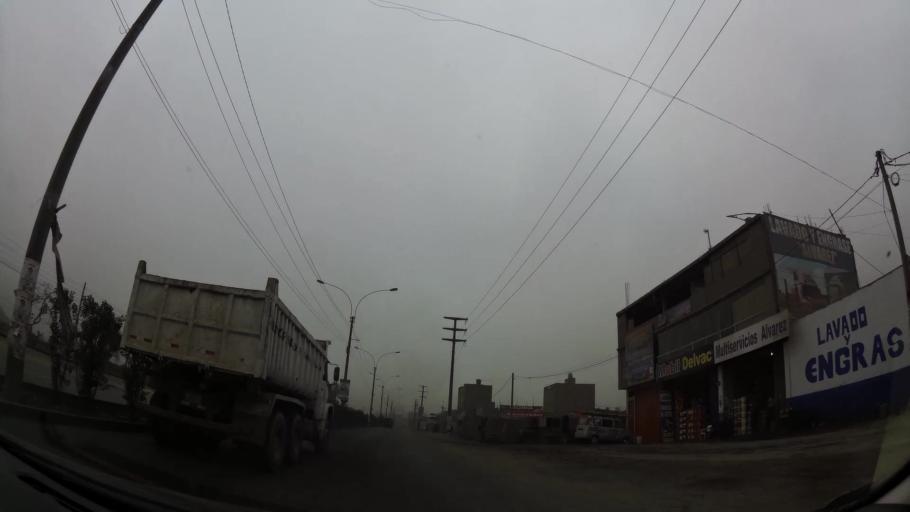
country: PE
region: Lima
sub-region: Lima
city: Santa Maria
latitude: -12.0067
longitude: -76.8516
